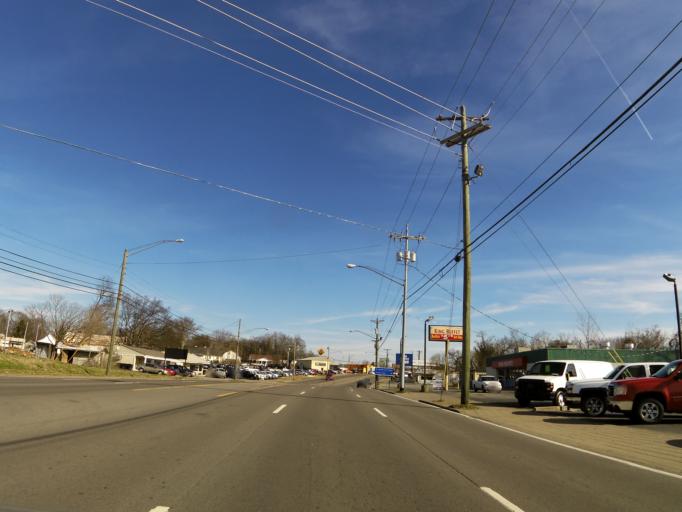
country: US
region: Tennessee
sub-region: Rutherford County
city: Murfreesboro
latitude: 35.8412
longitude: -86.3899
